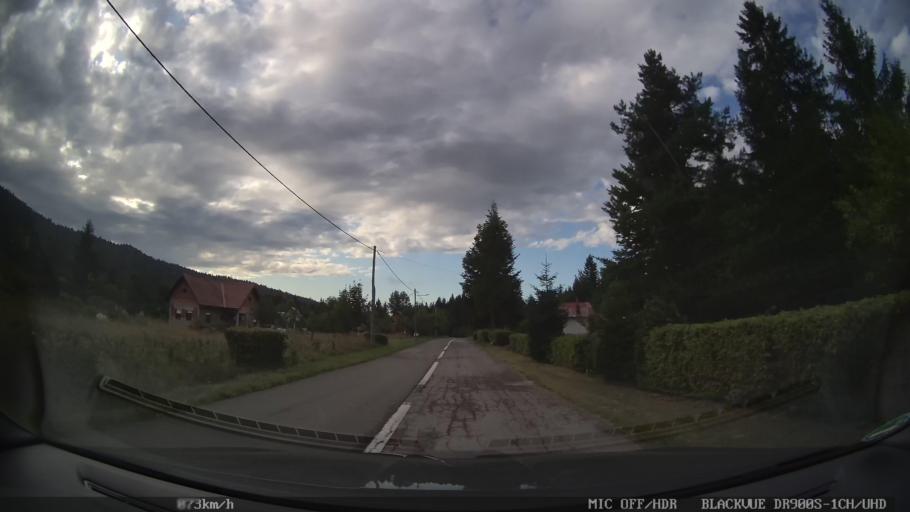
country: HR
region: Licko-Senjska
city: Jezerce
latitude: 44.9503
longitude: 15.5335
